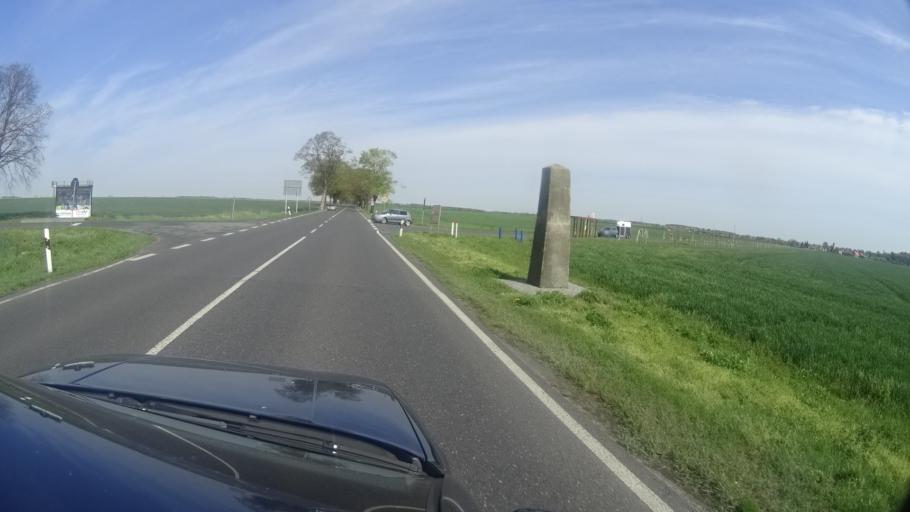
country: DE
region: Brandenburg
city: Pessin
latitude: 52.6649
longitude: 12.6297
